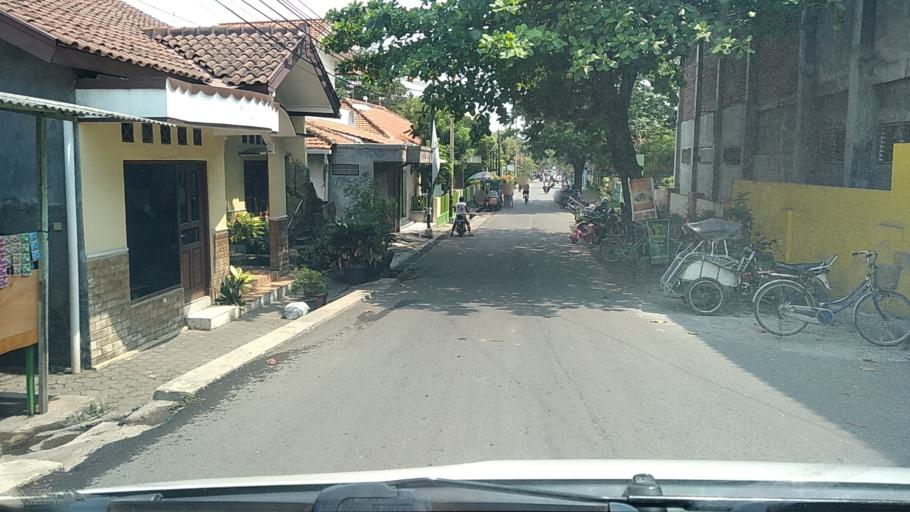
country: ID
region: Central Java
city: Semarang
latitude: -6.9822
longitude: 110.3512
